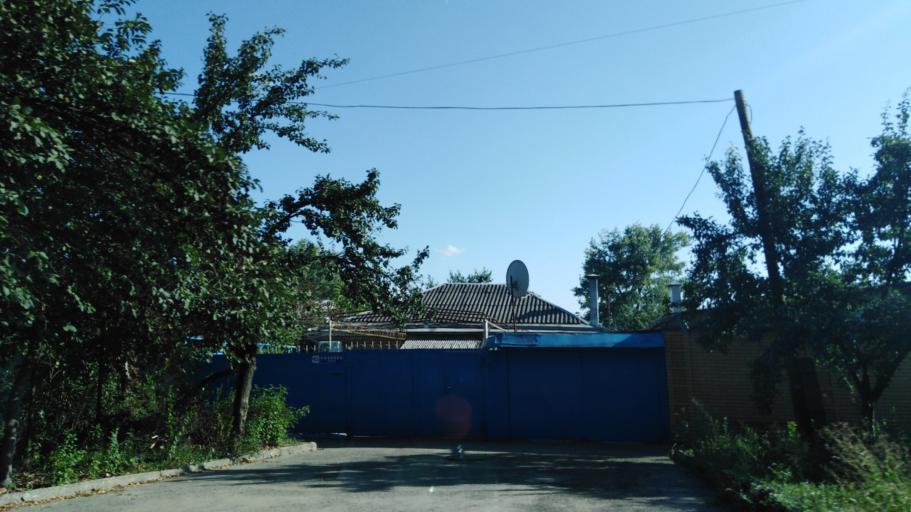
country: RU
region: Stavropol'skiy
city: Svobody
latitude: 44.0384
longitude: 43.0435
